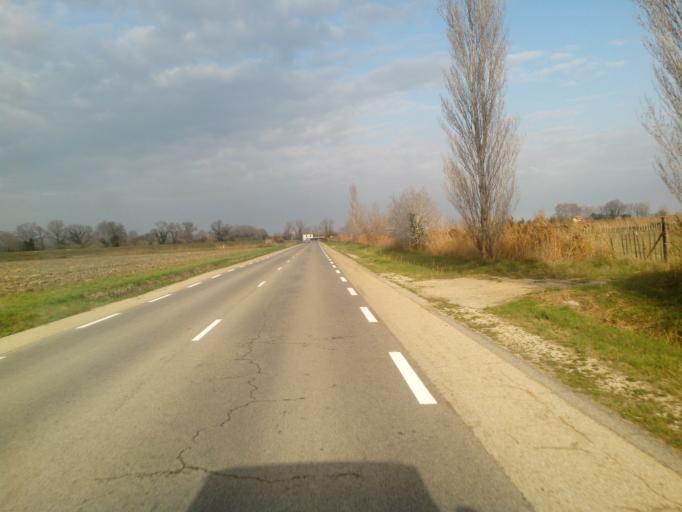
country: FR
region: Languedoc-Roussillon
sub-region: Departement du Gard
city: Saint-Gilles
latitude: 43.5991
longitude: 4.4728
